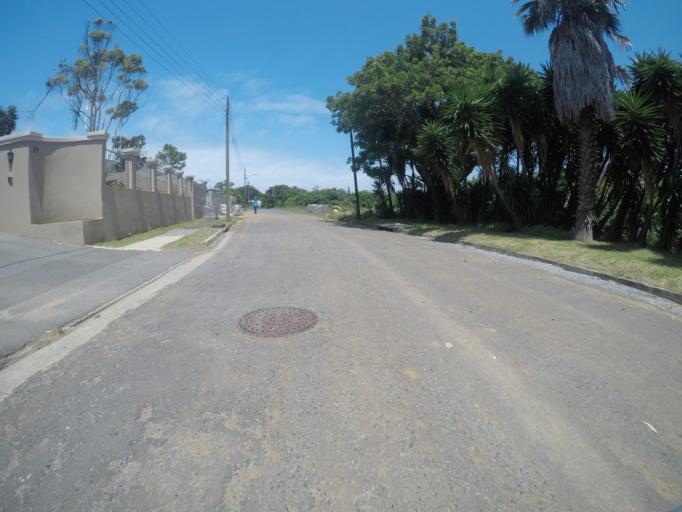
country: ZA
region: Eastern Cape
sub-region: Buffalo City Metropolitan Municipality
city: East London
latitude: -33.0038
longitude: 27.9175
